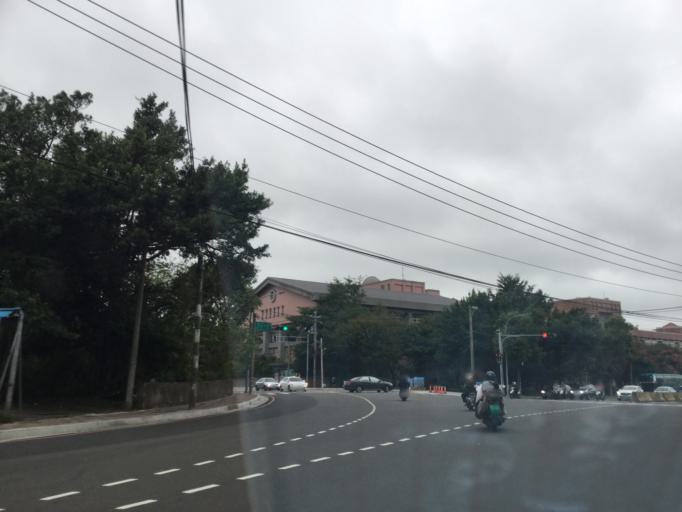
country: TW
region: Taiwan
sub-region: Hsinchu
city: Hsinchu
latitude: 24.7961
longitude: 121.0021
